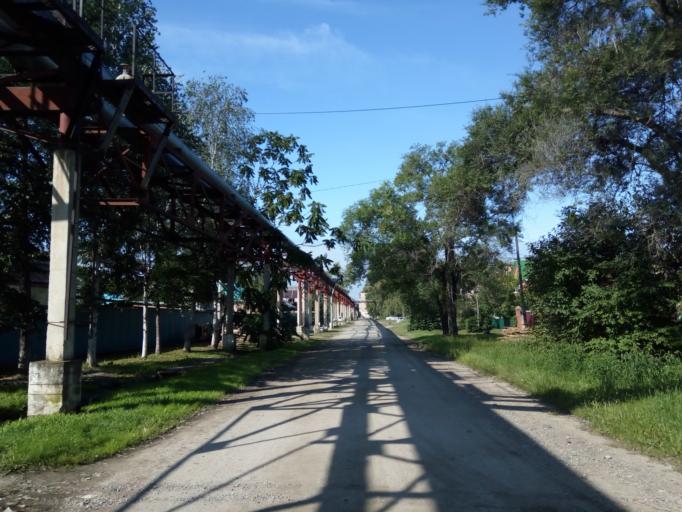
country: RU
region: Primorskiy
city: Dal'nerechensk
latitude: 45.9336
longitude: 133.7393
